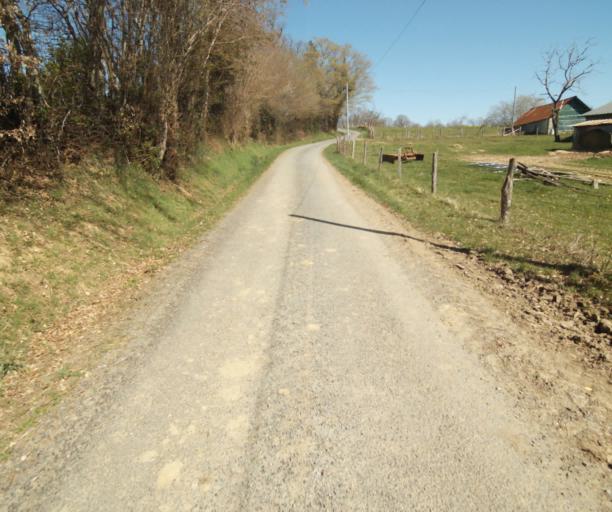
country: FR
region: Limousin
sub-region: Departement de la Correze
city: Saint-Mexant
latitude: 45.3074
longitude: 1.6424
